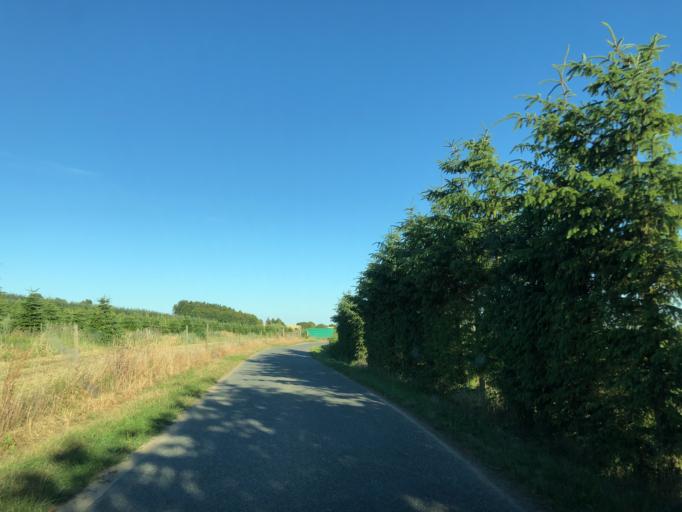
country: DK
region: Central Jutland
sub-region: Skanderborg Kommune
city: Ry
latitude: 55.9760
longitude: 9.8034
